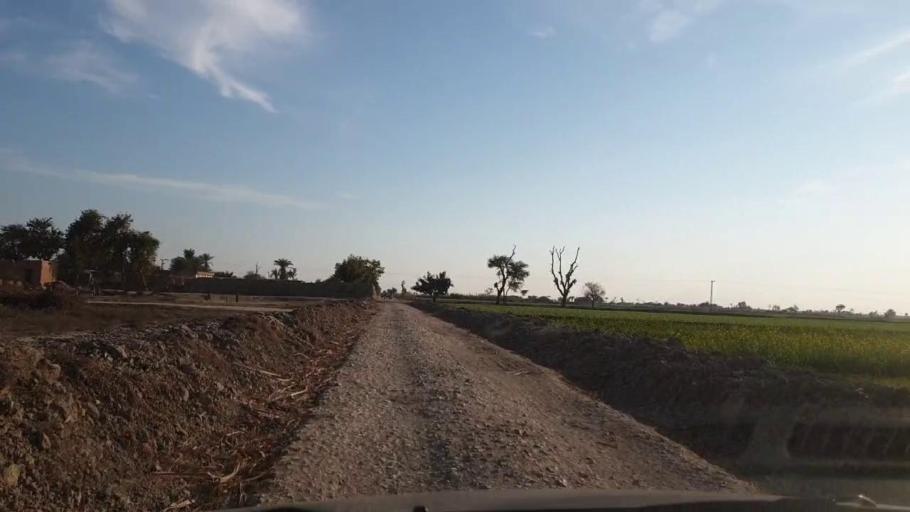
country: PK
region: Sindh
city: Khadro
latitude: 26.1722
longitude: 68.7530
